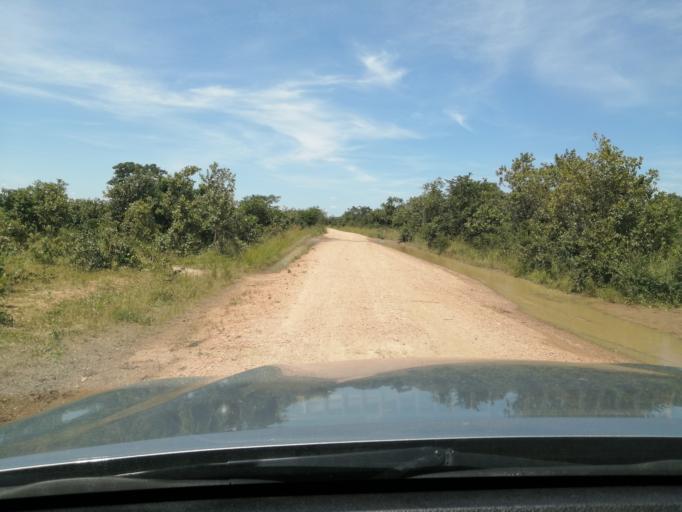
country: ZM
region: Central
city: Chibombo
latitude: -15.0494
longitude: 27.8249
